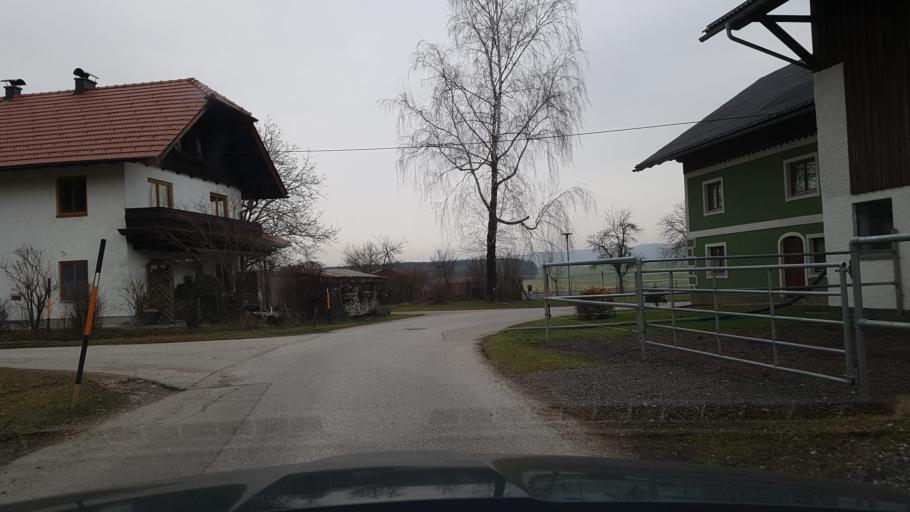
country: AT
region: Salzburg
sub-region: Politischer Bezirk Salzburg-Umgebung
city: Lamprechtshausen
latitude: 48.0114
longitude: 12.9597
